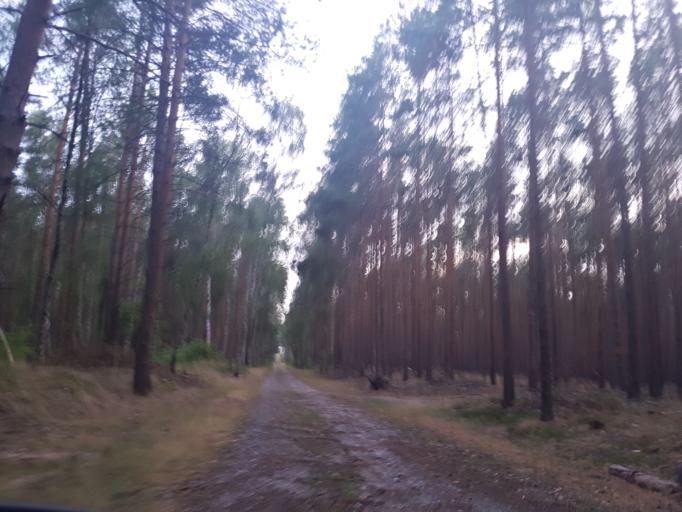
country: DE
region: Brandenburg
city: Trobitz
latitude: 51.5682
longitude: 13.4342
